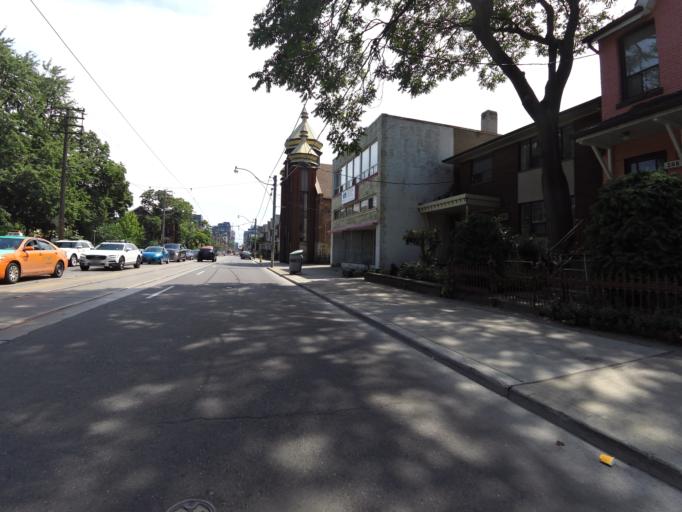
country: CA
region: Ontario
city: Toronto
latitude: 43.6505
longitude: -79.4054
